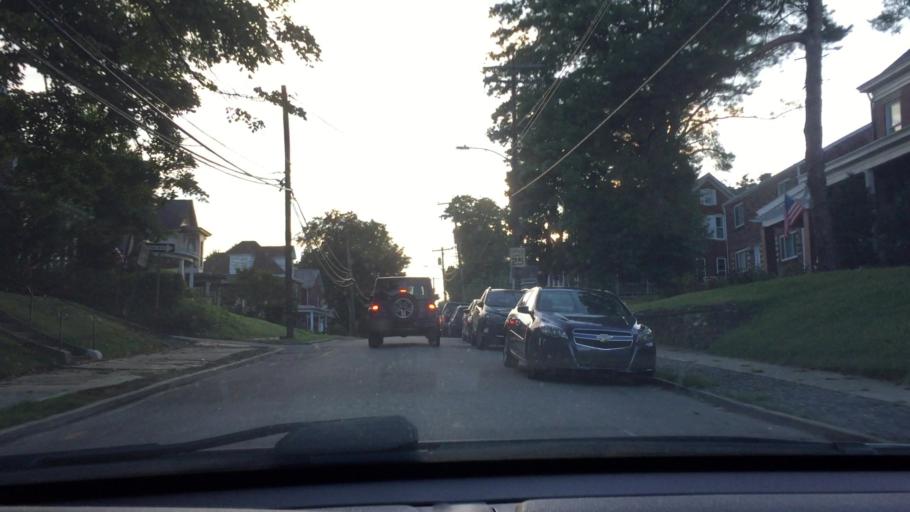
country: US
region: Pennsylvania
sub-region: Washington County
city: Canonsburg
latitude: 40.2597
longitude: -80.1901
